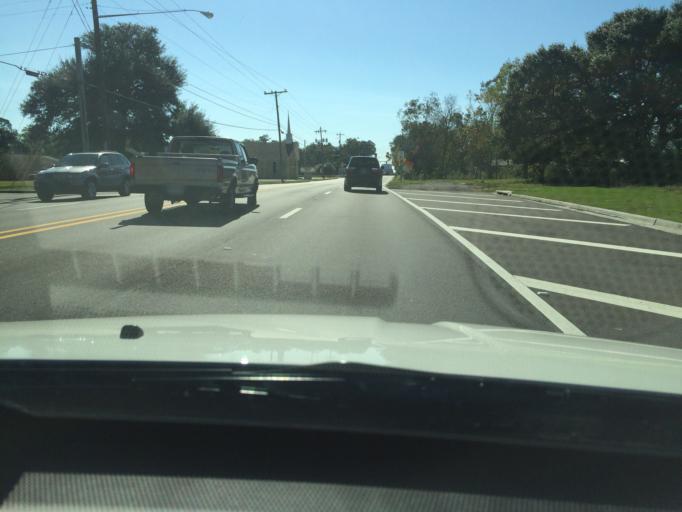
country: US
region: Mississippi
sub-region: Harrison County
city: D'Iberville
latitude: 30.4494
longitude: -88.8917
